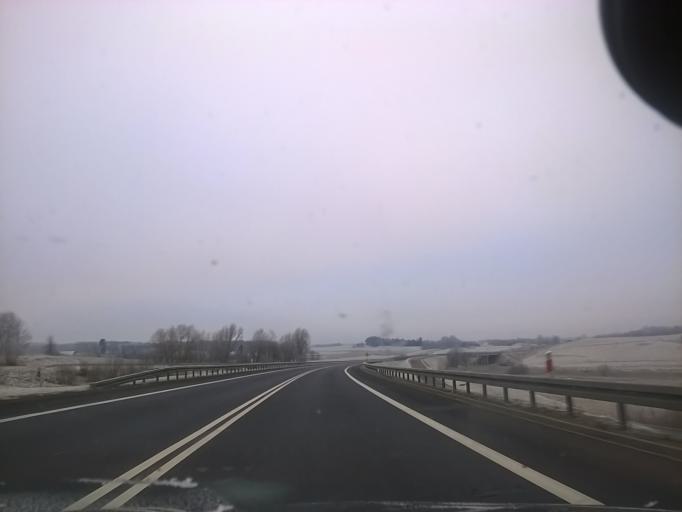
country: PL
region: Warmian-Masurian Voivodeship
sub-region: Powiat olsztynski
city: Biskupiec
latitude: 53.8342
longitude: 20.9222
